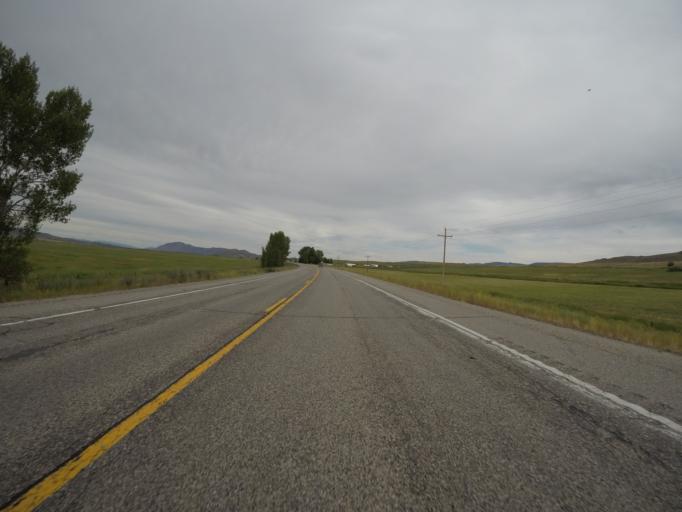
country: US
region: Utah
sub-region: Rich County
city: Randolph
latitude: 42.0214
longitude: -110.9332
